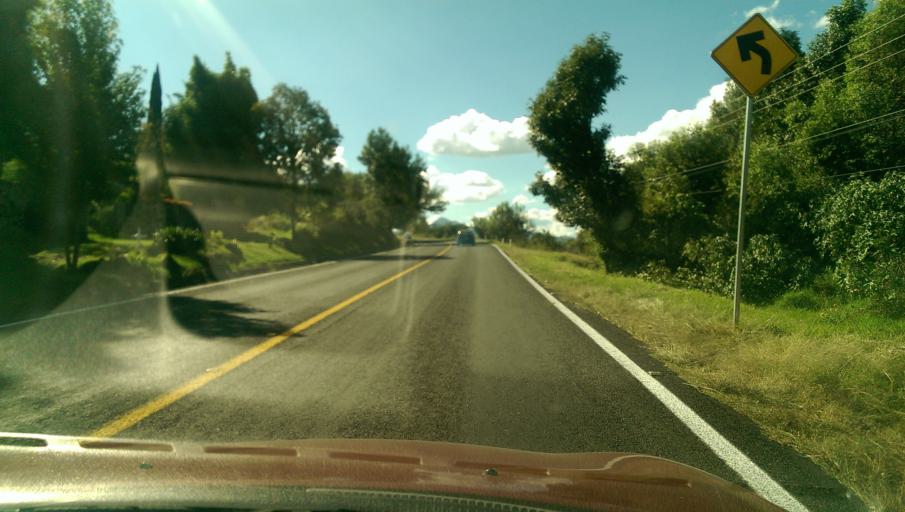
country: MX
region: Michoacan
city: Quiroga
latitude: 19.6401
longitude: -101.5436
